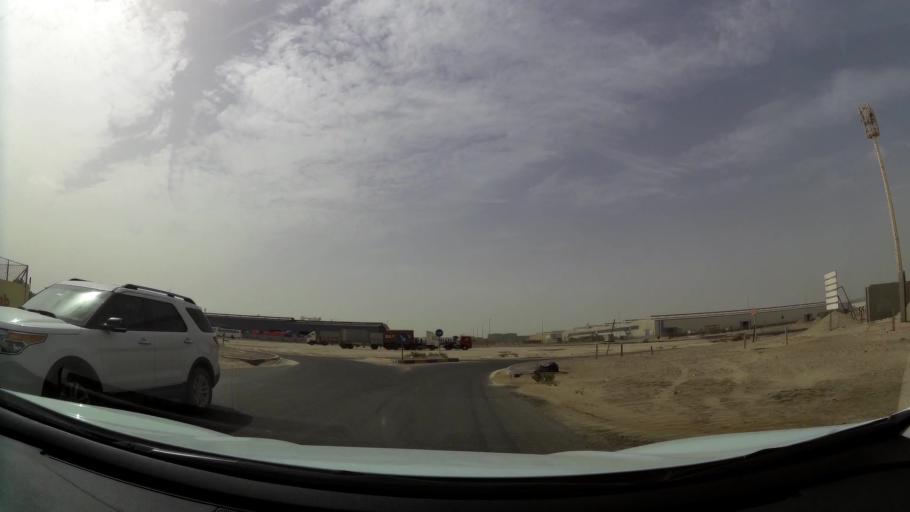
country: AE
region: Abu Dhabi
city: Abu Dhabi
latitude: 24.3288
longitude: 54.4847
